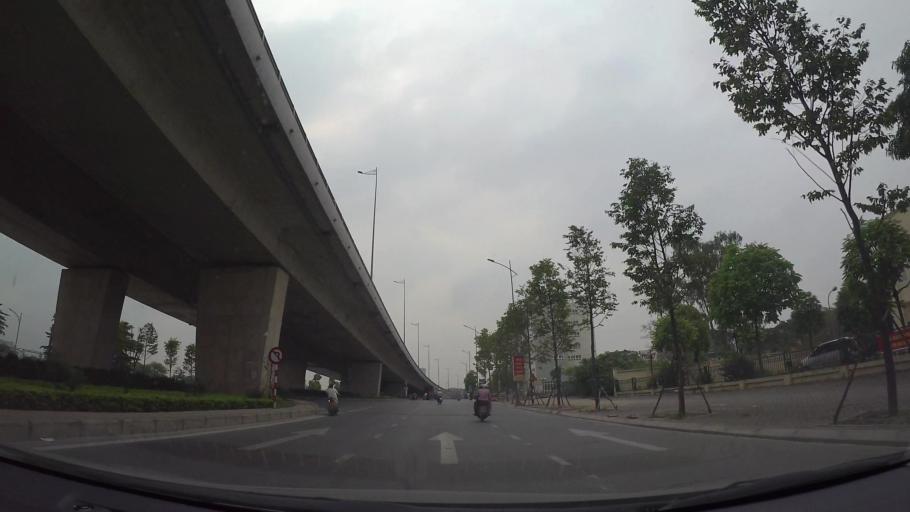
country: VN
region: Ha Noi
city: Hoan Kiem
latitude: 21.0577
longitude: 105.8854
